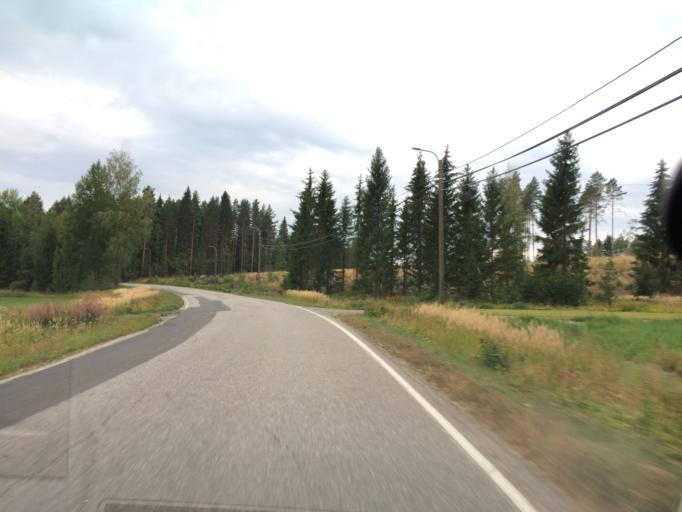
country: FI
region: Haeme
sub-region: Haemeenlinna
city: Tuulos
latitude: 61.1798
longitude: 24.7585
